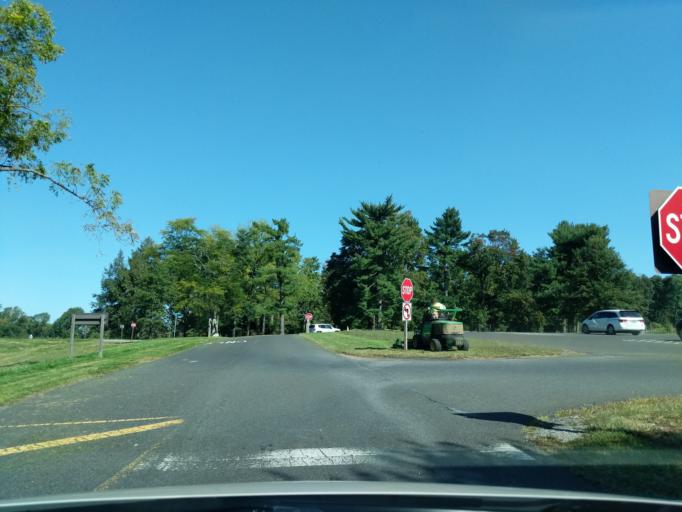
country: US
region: Pennsylvania
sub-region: Chester County
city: Chesterbrook
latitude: 40.1027
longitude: -75.4476
